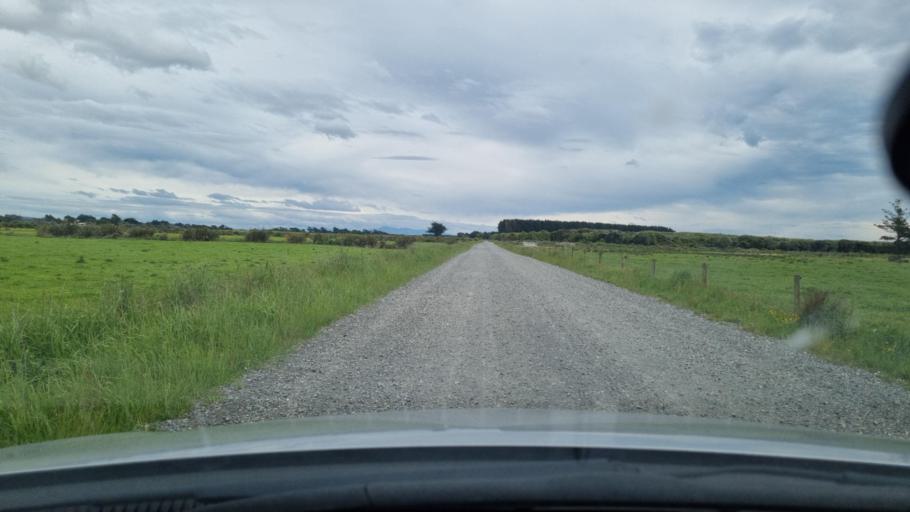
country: NZ
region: Southland
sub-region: Invercargill City
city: Invercargill
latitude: -46.4025
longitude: 168.2818
